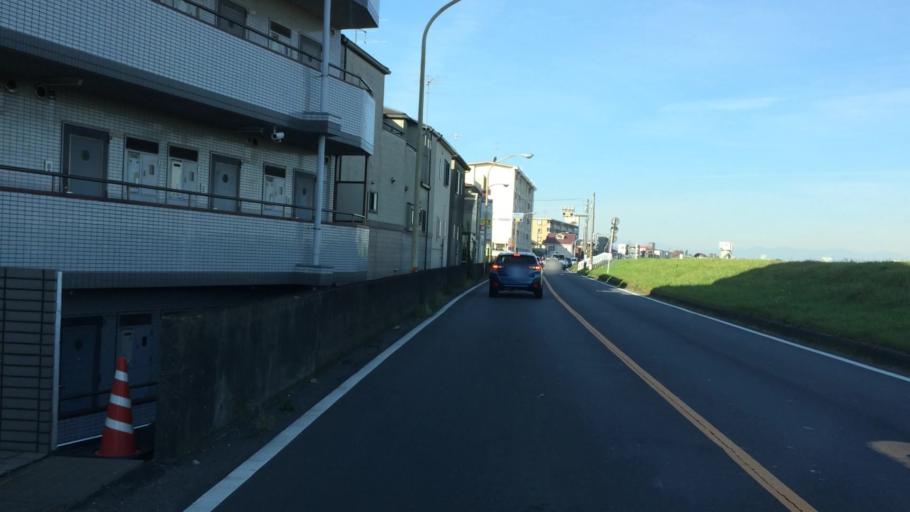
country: JP
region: Tokyo
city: Chofugaoka
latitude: 35.6335
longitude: 139.5518
